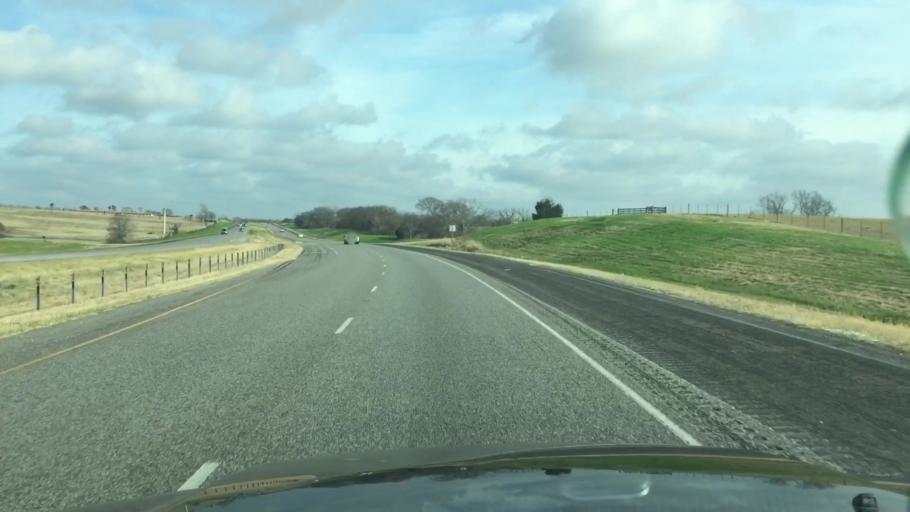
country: US
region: Texas
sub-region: Washington County
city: Brenham
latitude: 30.1372
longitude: -96.3495
